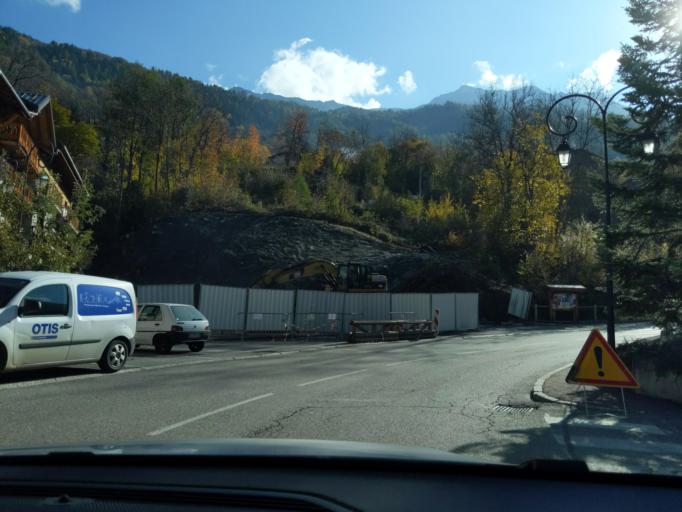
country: FR
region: Rhone-Alpes
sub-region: Departement de la Savoie
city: Seez
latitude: 45.5903
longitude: 6.8839
